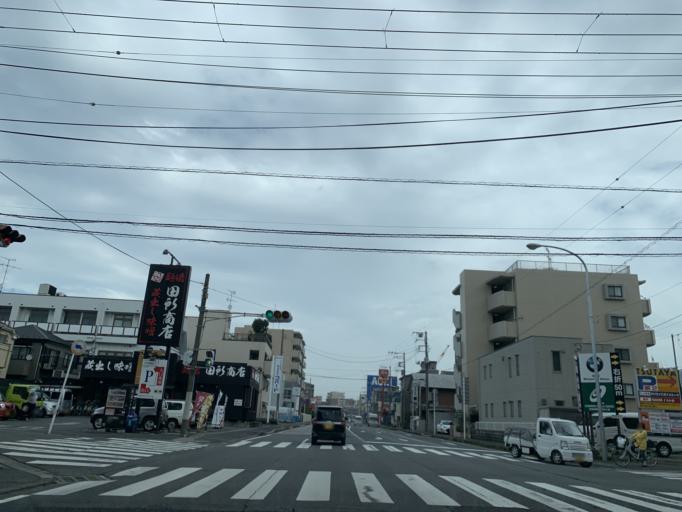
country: JP
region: Tokyo
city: Urayasu
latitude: 35.6876
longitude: 139.9183
